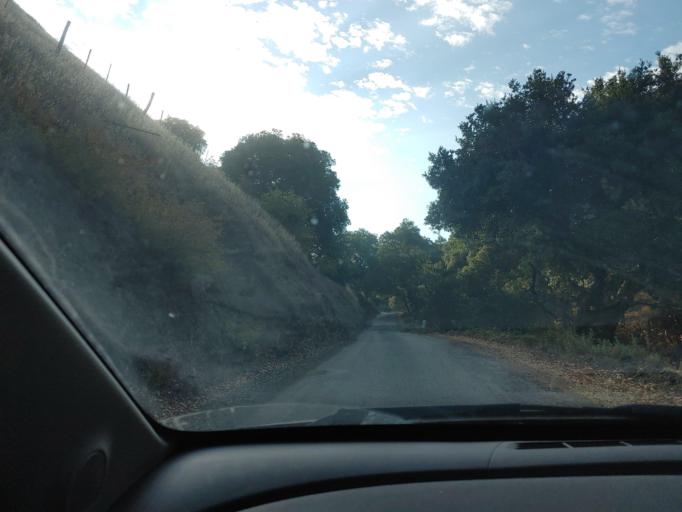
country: US
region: California
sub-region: San Benito County
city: Ridgemark
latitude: 36.7694
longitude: -121.2010
